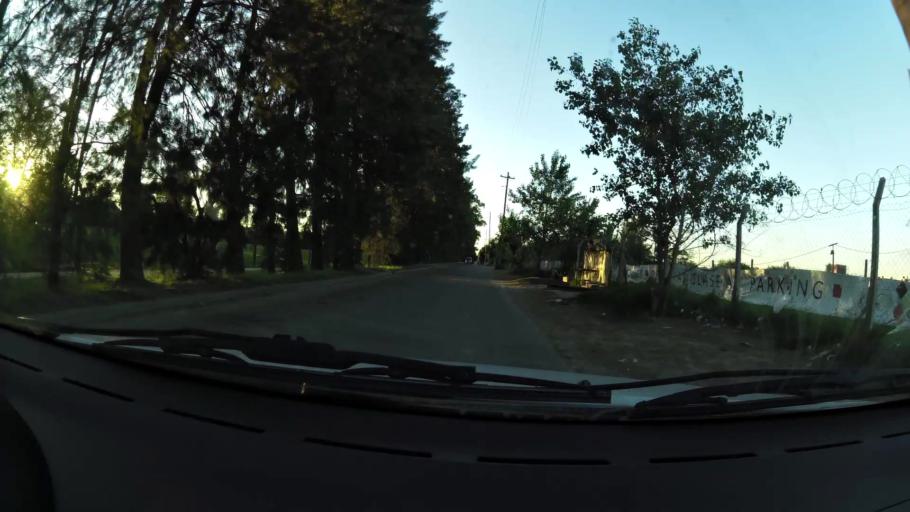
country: AR
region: Buenos Aires
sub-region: Partido de Quilmes
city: Quilmes
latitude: -34.8029
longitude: -58.1572
